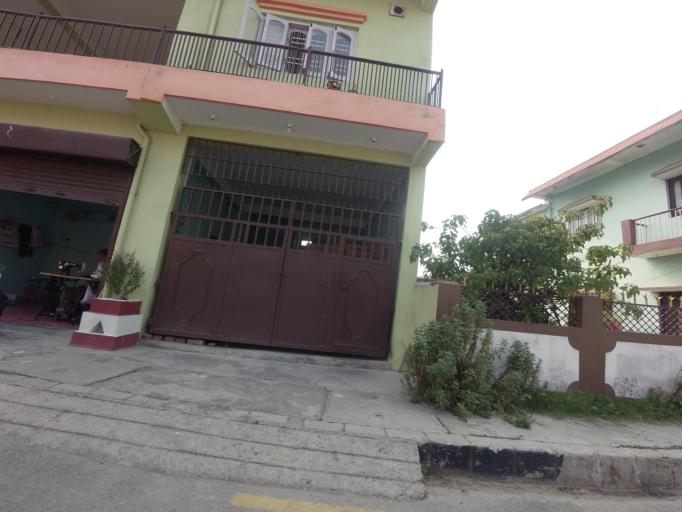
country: NP
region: Western Region
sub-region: Lumbini Zone
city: Bhairahawa
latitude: 27.5194
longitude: 83.4552
